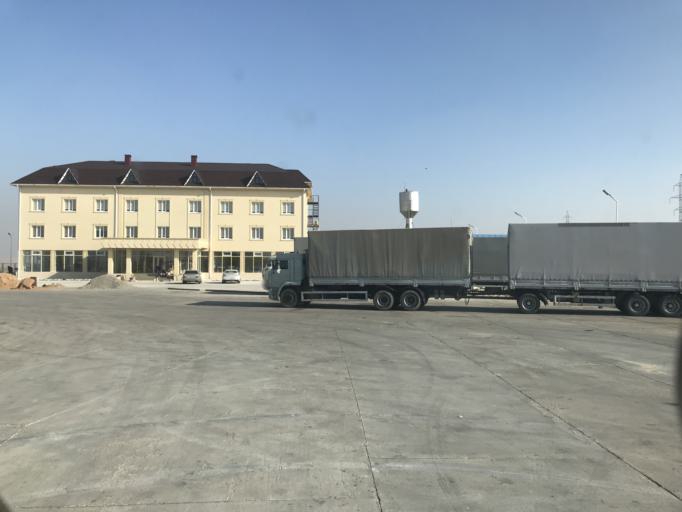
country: KZ
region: Ongtustik Qazaqstan
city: Shymkent
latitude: 42.4491
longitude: 69.6421
